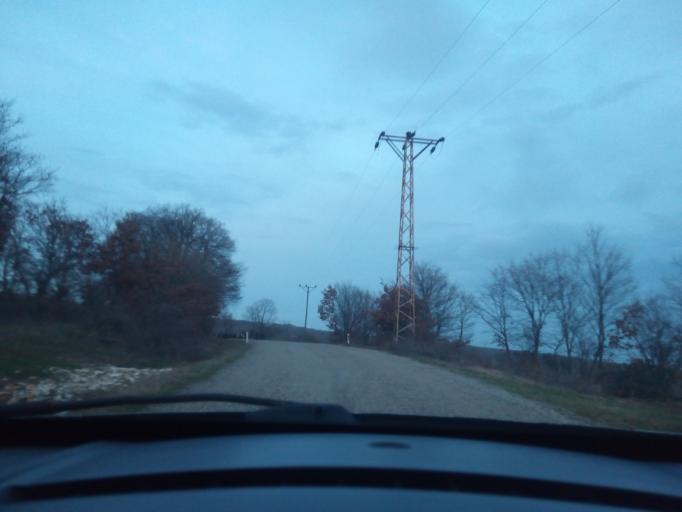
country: TR
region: Balikesir
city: Omerkoy
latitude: 39.9060
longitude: 28.0362
